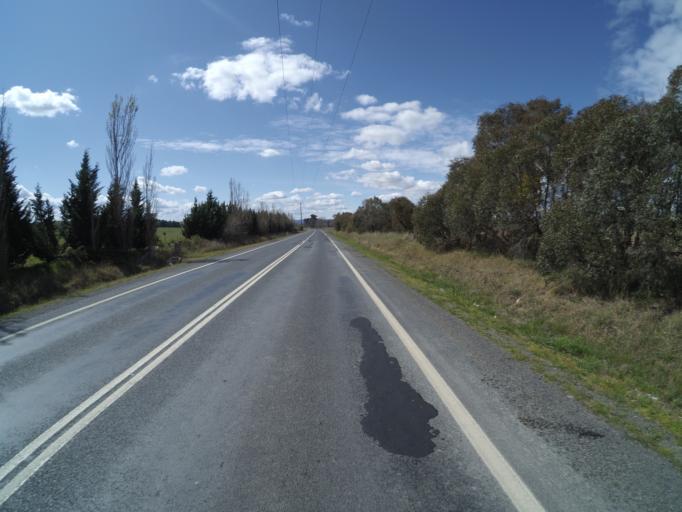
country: AU
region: New South Wales
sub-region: Goulburn Mulwaree
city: Goulburn
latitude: -34.7920
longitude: 149.6972
